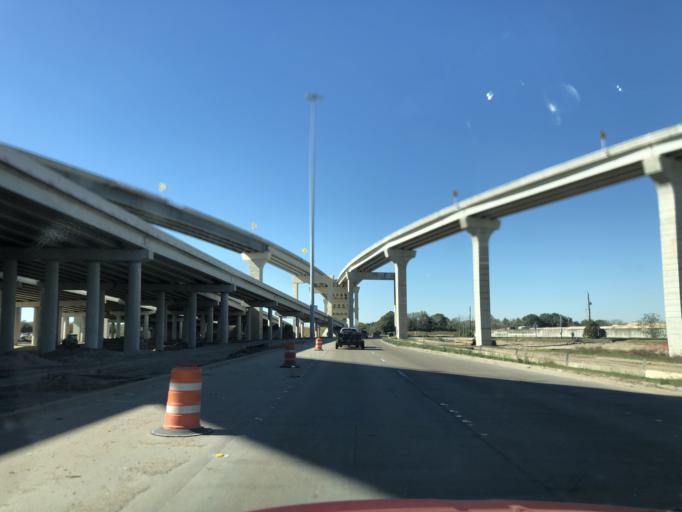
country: US
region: Texas
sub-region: Brazoria County
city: Brookside Village
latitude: 29.5978
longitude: -95.3879
